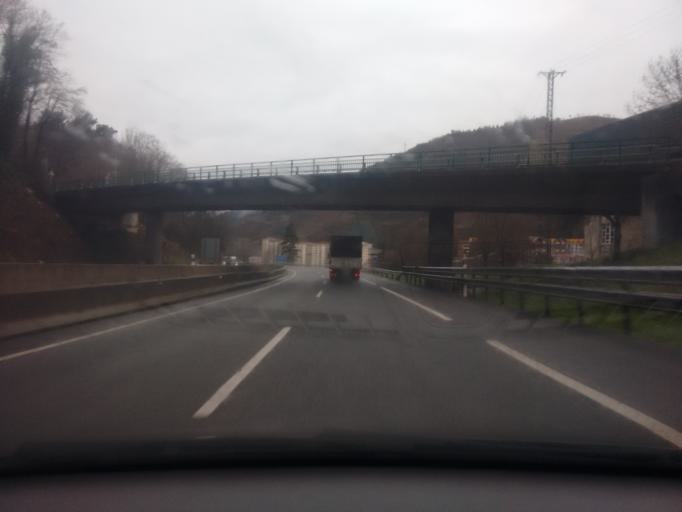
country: ES
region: Basque Country
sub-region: Provincia de Guipuzcoa
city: Eibar
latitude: 43.1814
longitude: -2.4785
